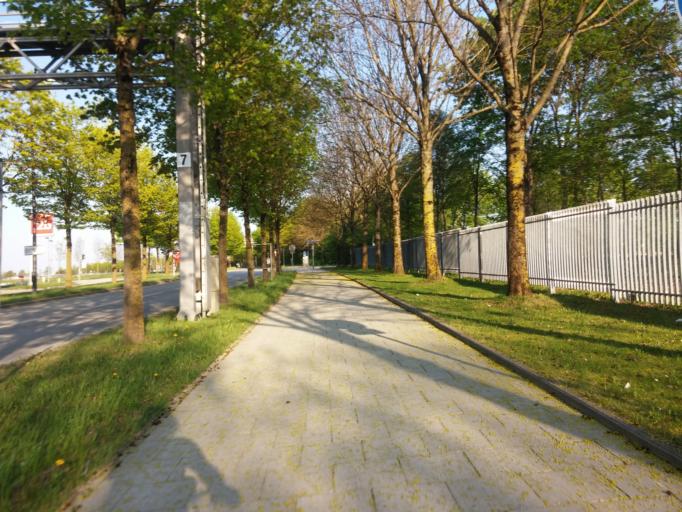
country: DE
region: Bavaria
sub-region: Upper Bavaria
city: Feldkirchen
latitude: 48.1383
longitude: 11.7059
